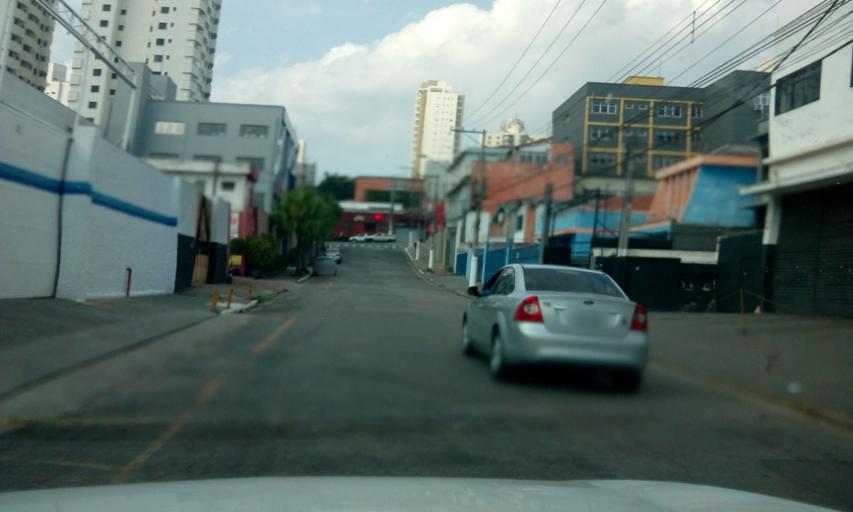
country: BR
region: Sao Paulo
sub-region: Osasco
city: Osasco
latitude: -23.5348
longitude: -46.7287
